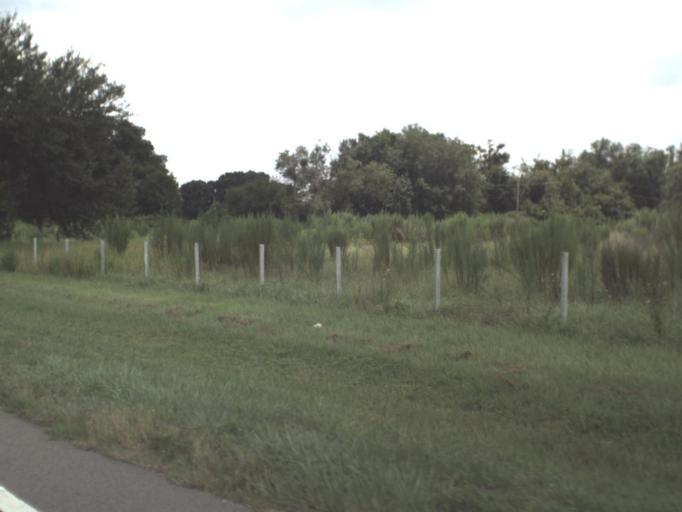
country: US
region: Florida
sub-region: Hillsborough County
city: Balm
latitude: 27.7049
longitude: -82.2377
